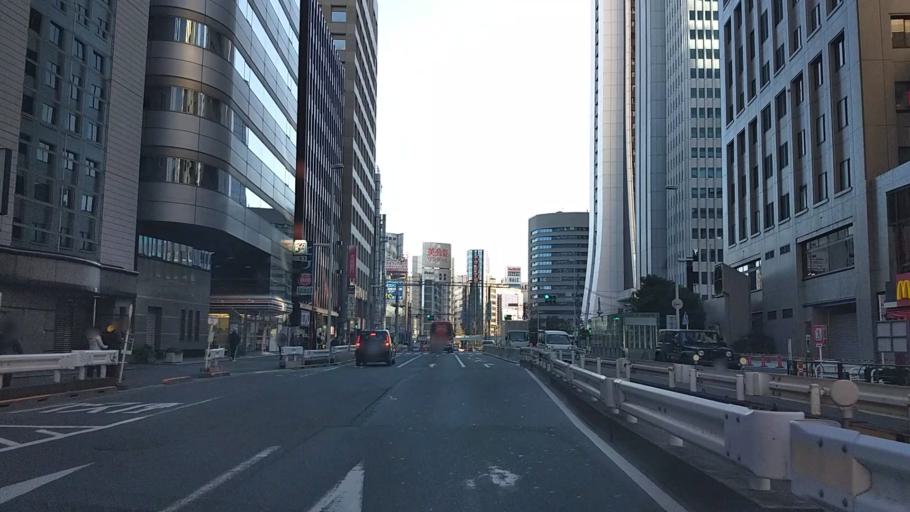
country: JP
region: Tokyo
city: Tokyo
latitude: 35.6940
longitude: 139.6942
